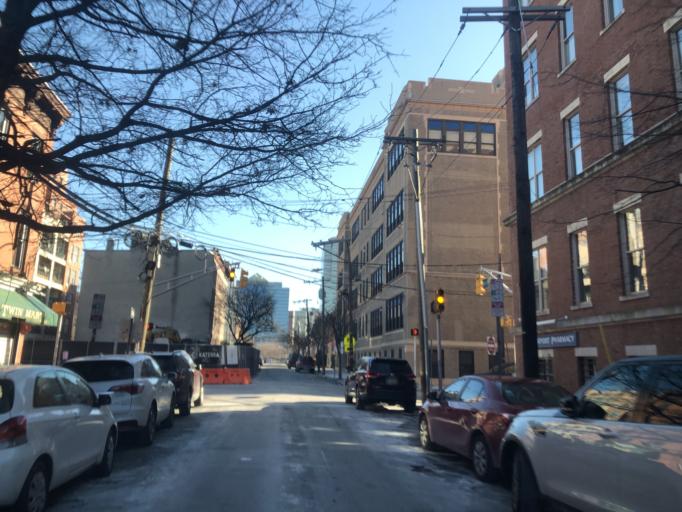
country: US
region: New Jersey
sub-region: Hudson County
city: Hoboken
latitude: 40.7283
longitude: -74.0437
